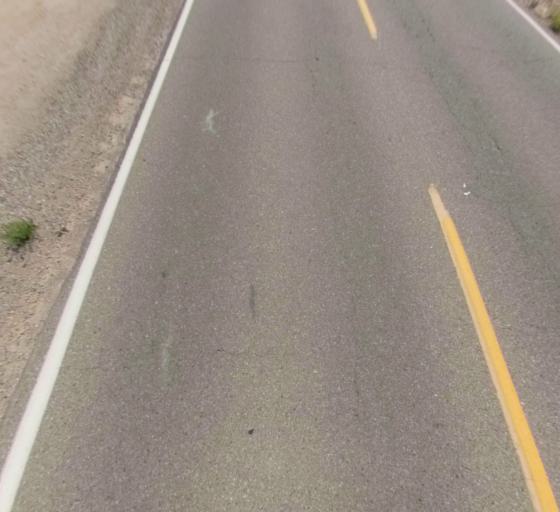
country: US
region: California
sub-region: Madera County
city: Parkwood
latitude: 36.8481
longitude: -120.1077
